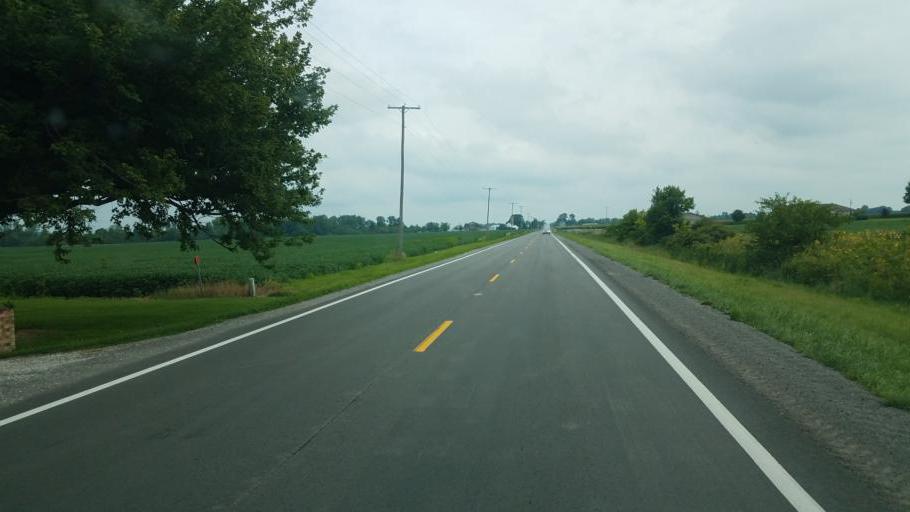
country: US
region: Ohio
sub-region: Marion County
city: Marion
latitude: 40.5982
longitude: -83.0352
